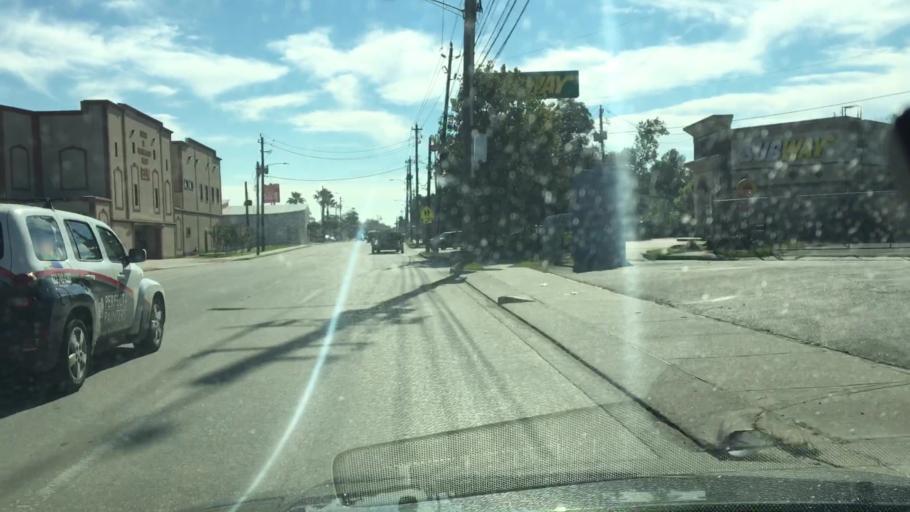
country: US
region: Texas
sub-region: Harris County
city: Houston
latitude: 29.7921
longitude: -95.3748
